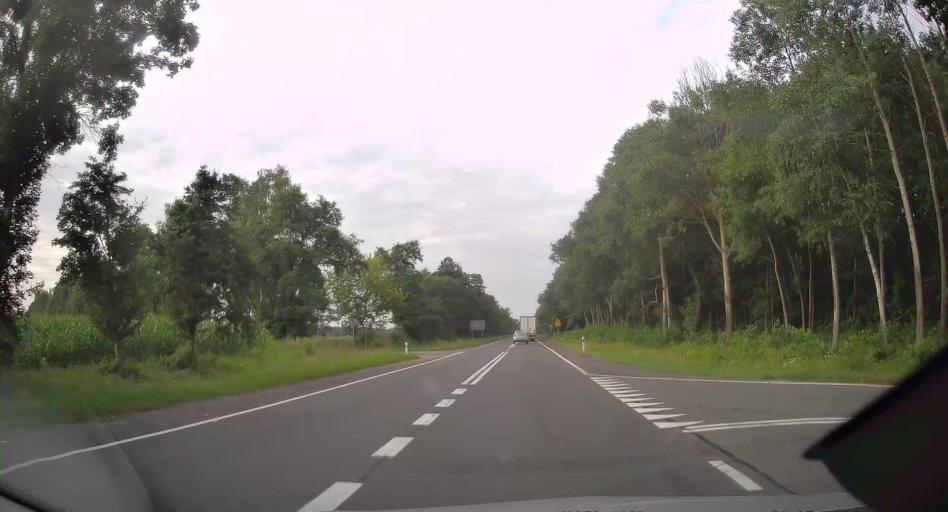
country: PL
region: Lodz Voivodeship
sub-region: Powiat radomszczanski
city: Plawno
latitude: 50.9610
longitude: 19.4046
